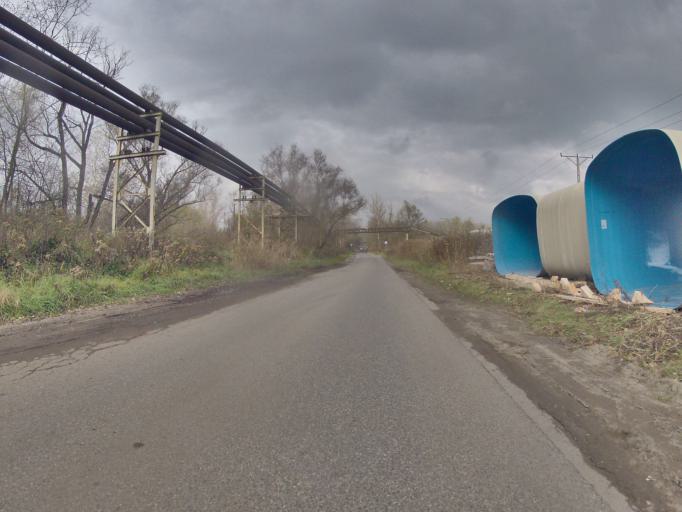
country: PL
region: Lesser Poland Voivodeship
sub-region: Powiat wielicki
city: Wegrzce Wielkie
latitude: 50.0618
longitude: 20.1025
